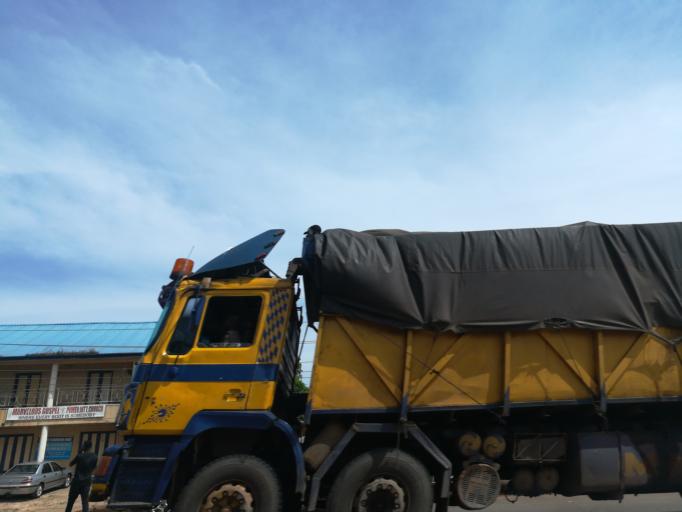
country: NG
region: Plateau
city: Bukuru
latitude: 9.7886
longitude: 8.8589
